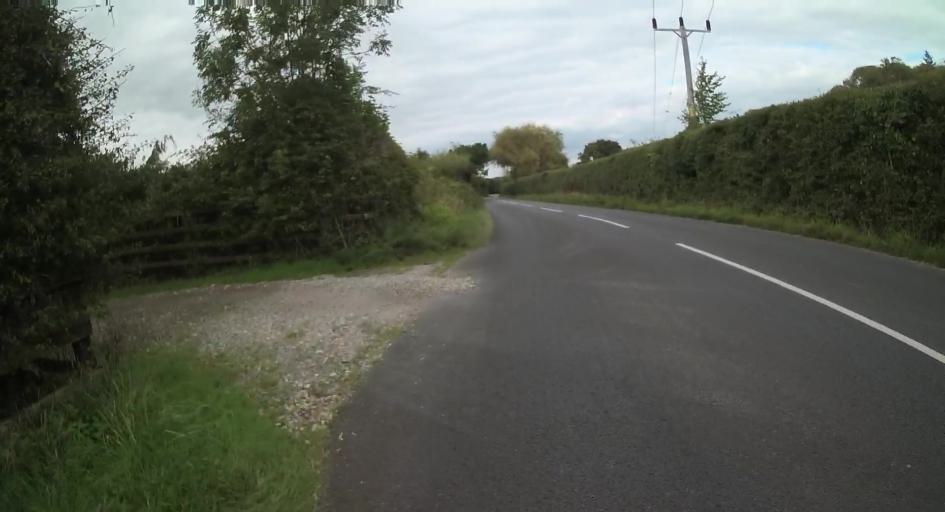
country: GB
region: England
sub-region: Isle of Wight
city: Freshwater
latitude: 50.6879
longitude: -1.4915
